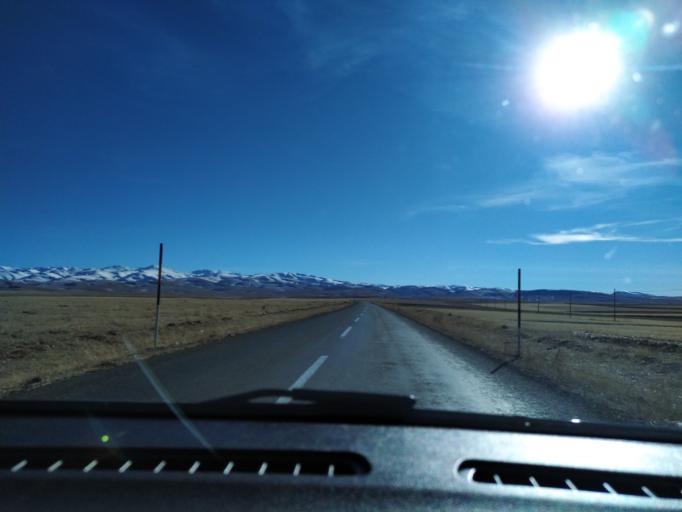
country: TR
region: Kayseri
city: Orensehir
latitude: 38.8964
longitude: 36.7294
